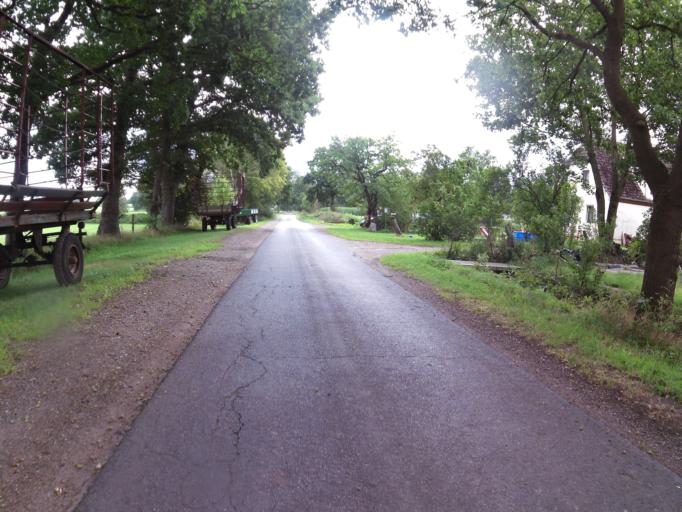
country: DE
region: Lower Saxony
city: Schiffdorf
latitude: 53.5003
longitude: 8.7028
